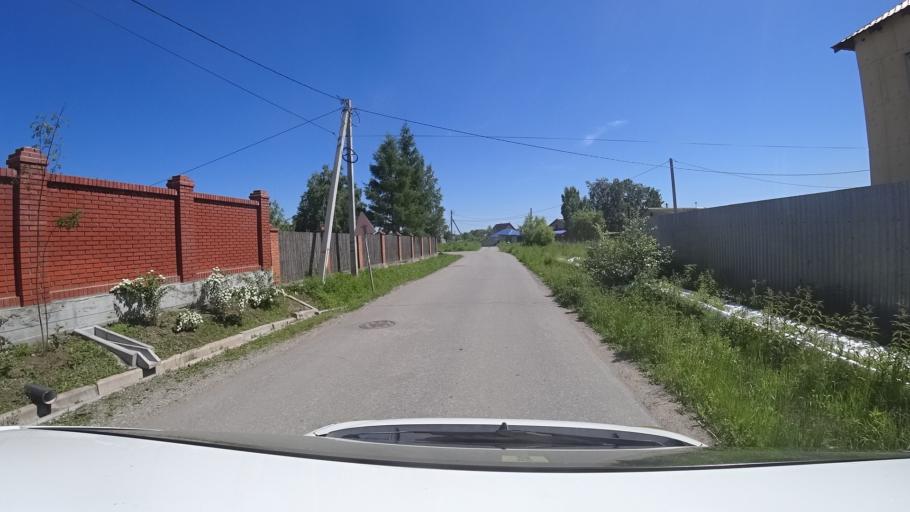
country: RU
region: Khabarovsk Krai
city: Topolevo
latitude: 48.5033
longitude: 135.1762
